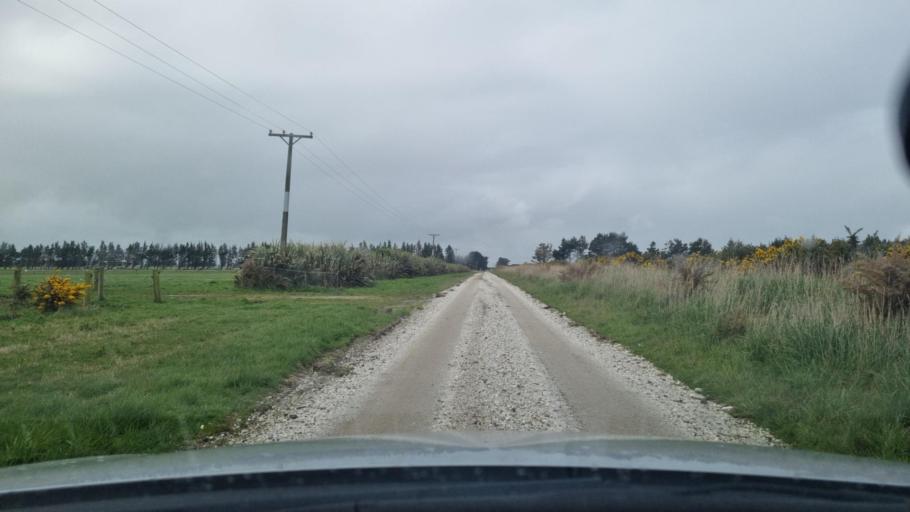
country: NZ
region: Southland
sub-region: Invercargill City
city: Invercargill
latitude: -46.4952
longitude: 168.4212
